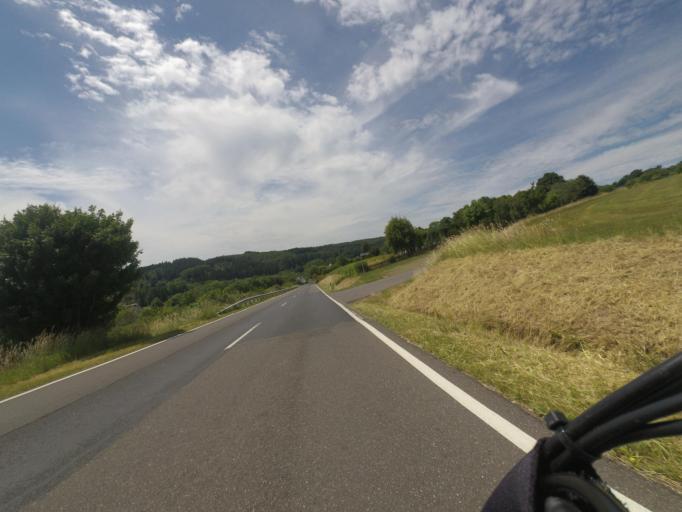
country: DE
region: Rheinland-Pfalz
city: Stadtkyll
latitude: 50.3564
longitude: 6.5285
